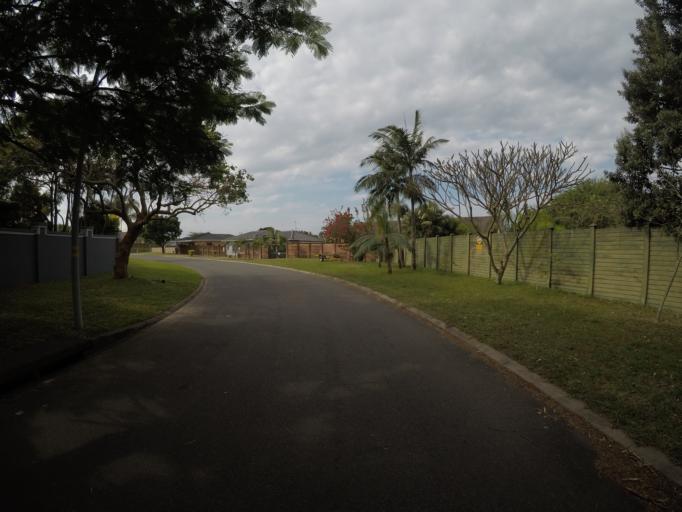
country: ZA
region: KwaZulu-Natal
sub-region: uThungulu District Municipality
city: Richards Bay
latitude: -28.7378
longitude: 32.0899
